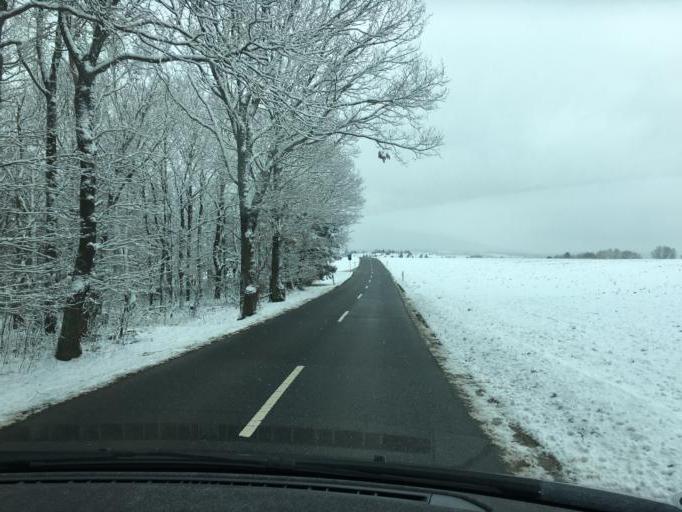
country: DE
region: North Rhine-Westphalia
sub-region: Regierungsbezirk Koln
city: Hurtgenwald
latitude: 50.7086
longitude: 6.4119
